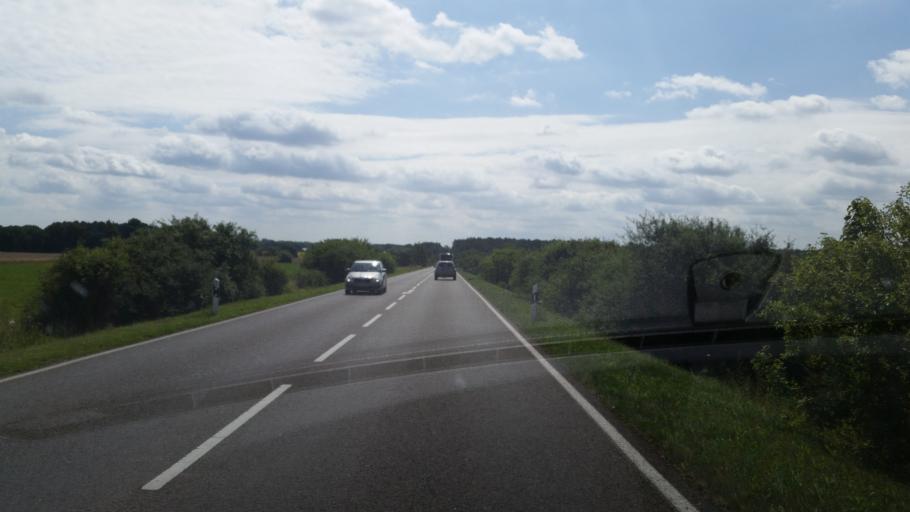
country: DE
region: Saxony
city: Bernsdorf
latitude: 51.3298
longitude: 14.0753
